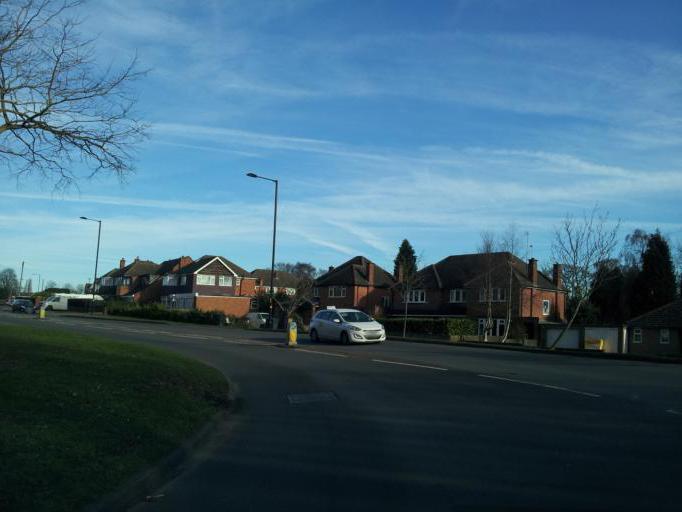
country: GB
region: England
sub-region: City and Borough of Birmingham
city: Sutton Coldfield
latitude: 52.5856
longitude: -1.8194
